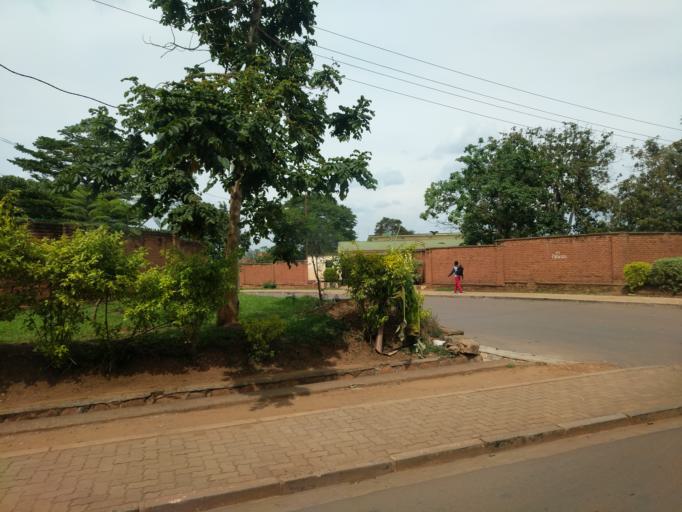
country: RW
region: Kigali
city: Kigali
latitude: -1.9740
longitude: 30.1050
